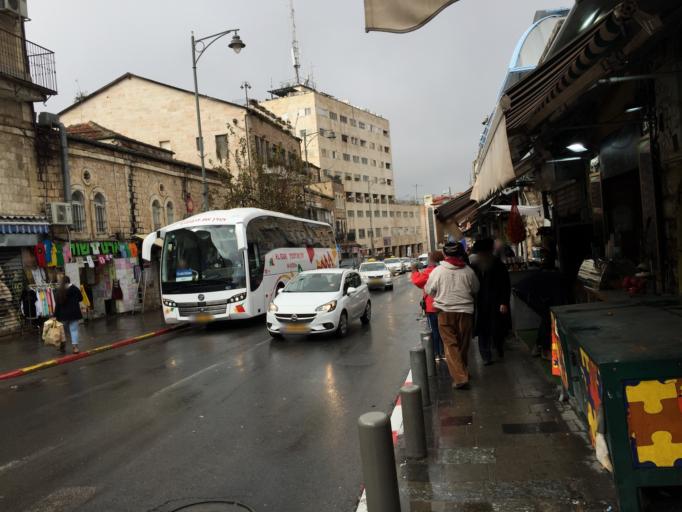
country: IL
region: Jerusalem
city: West Jerusalem
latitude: 31.7839
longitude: 35.2130
